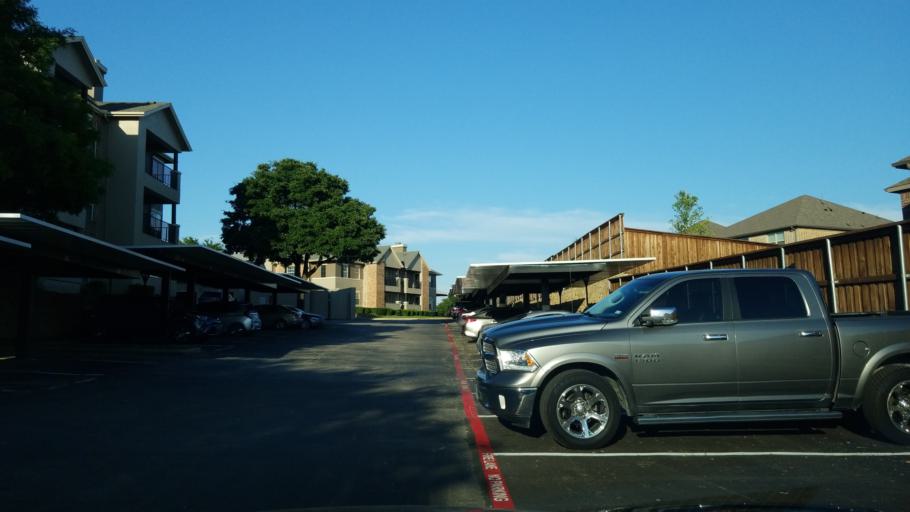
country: US
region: Texas
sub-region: Dallas County
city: Coppell
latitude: 32.9092
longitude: -96.9851
